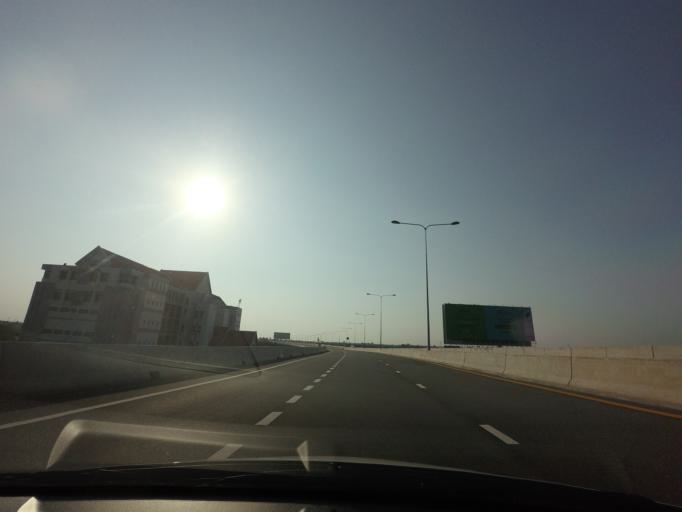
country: TH
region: Bangkok
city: Taling Chan
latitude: 13.7973
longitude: 100.4302
